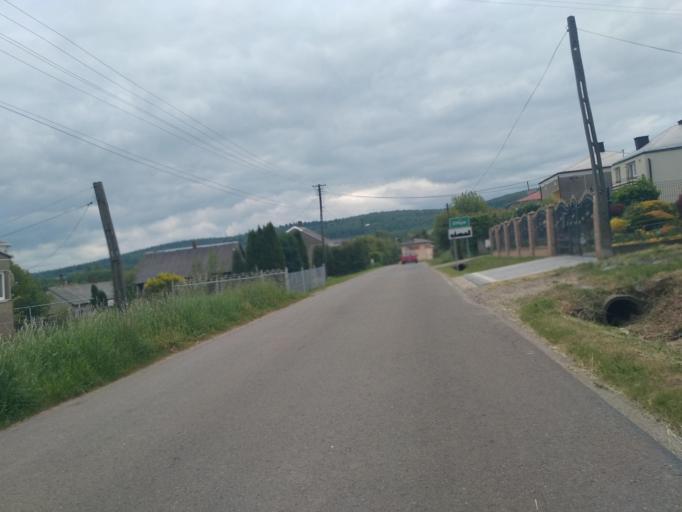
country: PL
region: Subcarpathian Voivodeship
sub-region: Powiat krosnienski
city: Jedlicze
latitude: 49.6977
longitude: 21.6396
